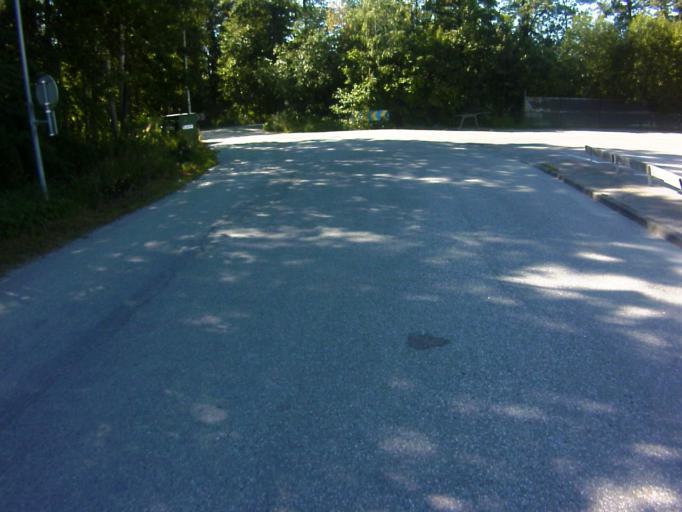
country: SE
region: Soedermanland
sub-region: Eskilstuna Kommun
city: Eskilstuna
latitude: 59.3856
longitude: 16.4867
